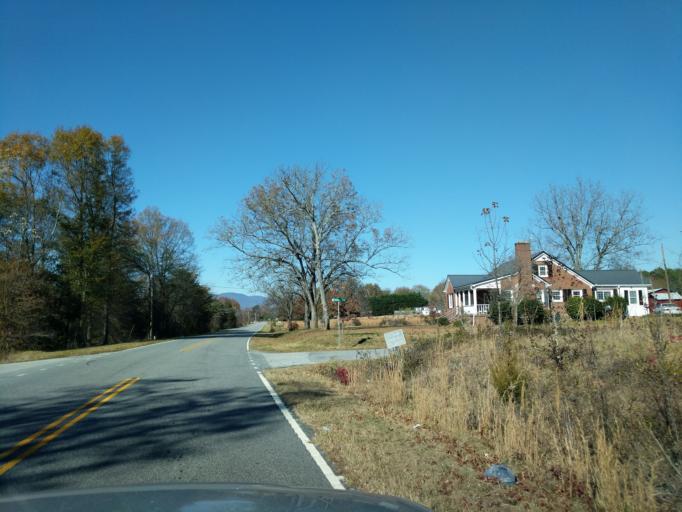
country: US
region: South Carolina
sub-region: Spartanburg County
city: Inman Mills
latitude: 35.0657
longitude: -82.1872
